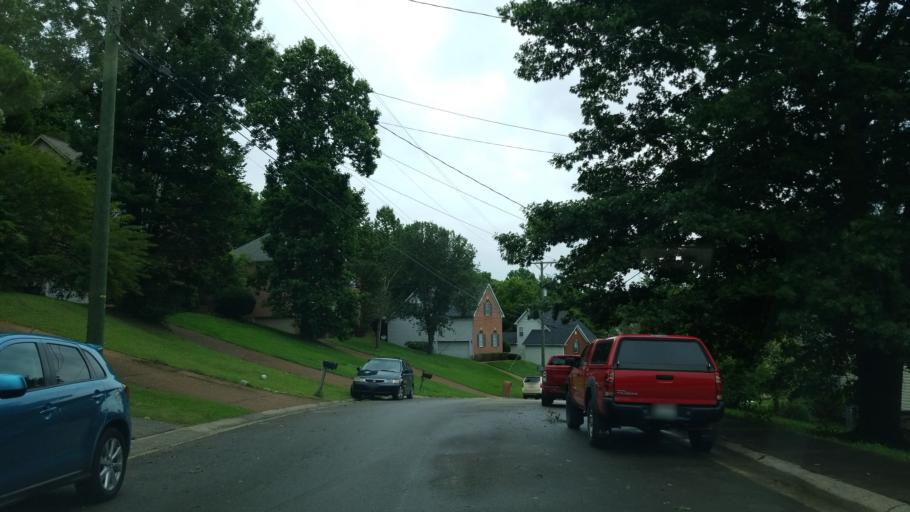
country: US
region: Tennessee
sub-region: Rutherford County
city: La Vergne
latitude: 36.0619
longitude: -86.6669
